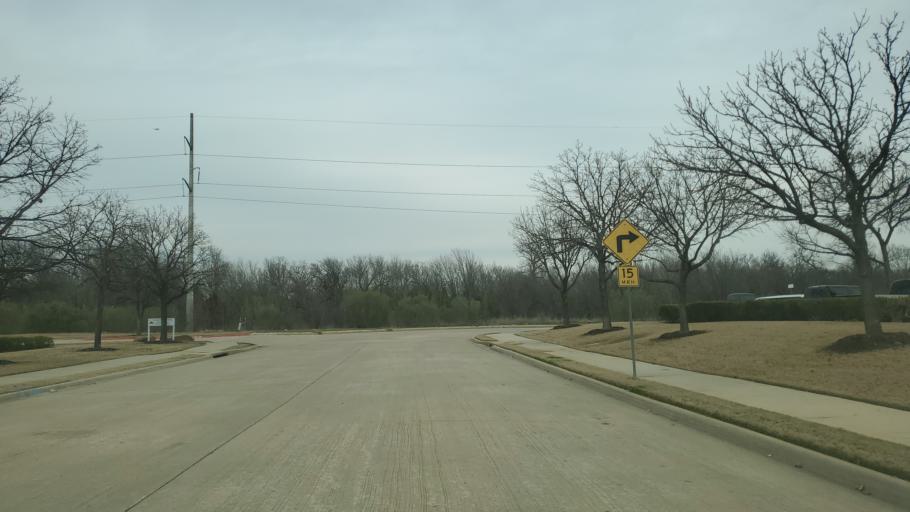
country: US
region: Texas
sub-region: Dallas County
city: Coppell
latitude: 32.9882
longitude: -97.0219
